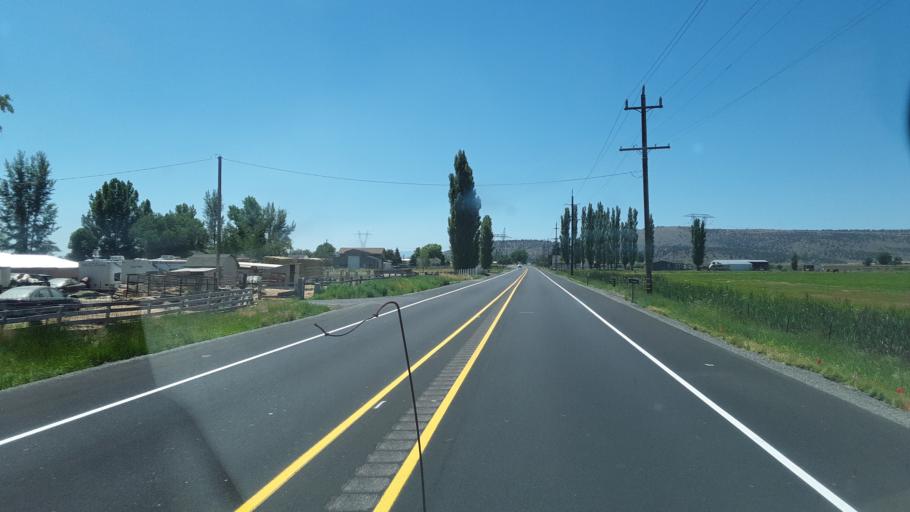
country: US
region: Oregon
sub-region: Klamath County
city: Altamont
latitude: 42.1088
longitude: -121.6986
